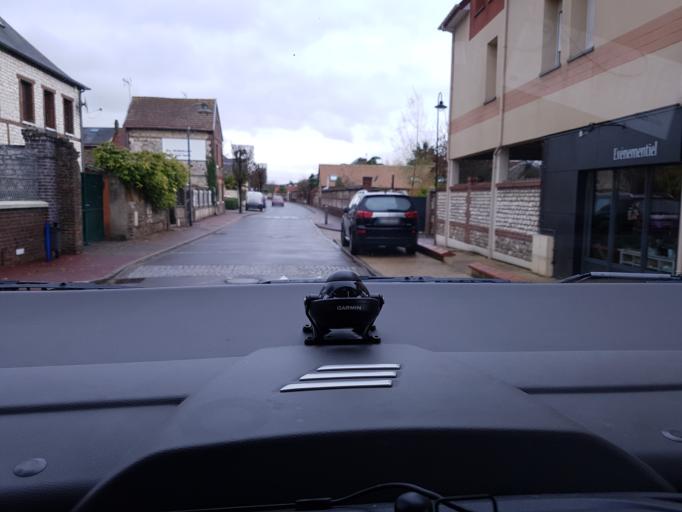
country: FR
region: Haute-Normandie
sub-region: Departement de l'Eure
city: Alizay
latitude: 49.3210
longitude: 1.1799
